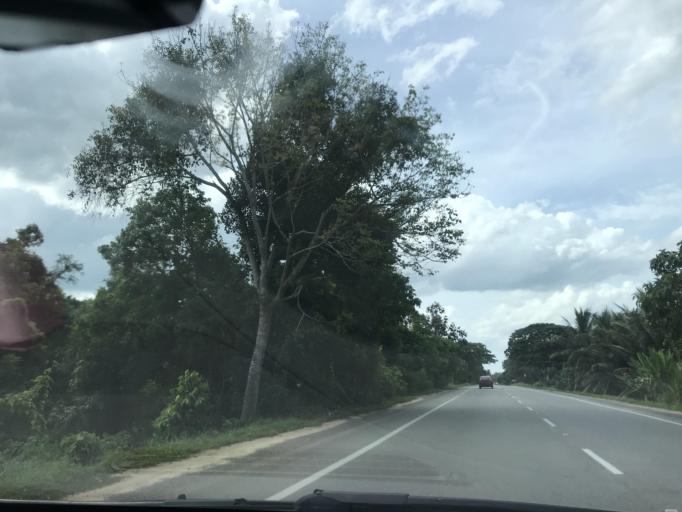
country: MY
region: Kelantan
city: Kampong Pangkal Kalong
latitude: 5.8995
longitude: 102.1855
